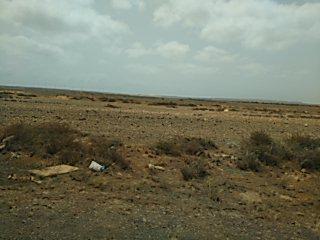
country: CV
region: Sal
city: Espargos
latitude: 16.7049
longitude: -22.9394
